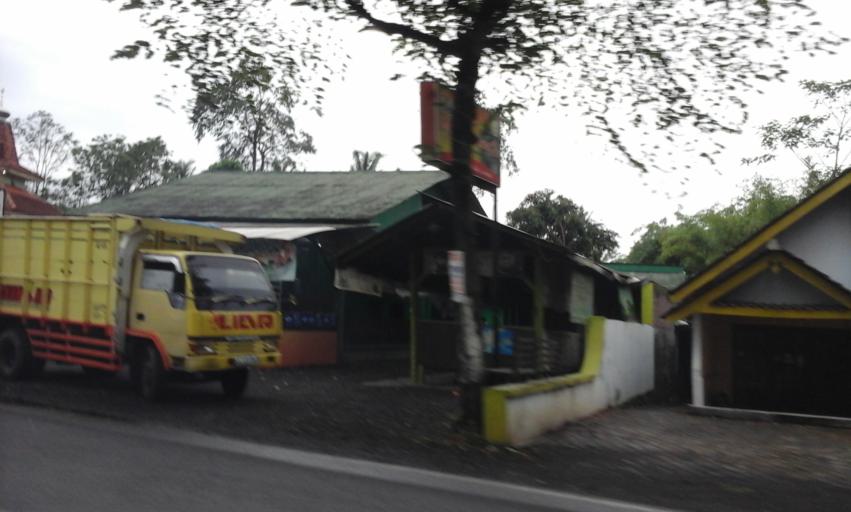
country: ID
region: East Java
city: Krajan Baru
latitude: -8.0930
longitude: 113.2618
